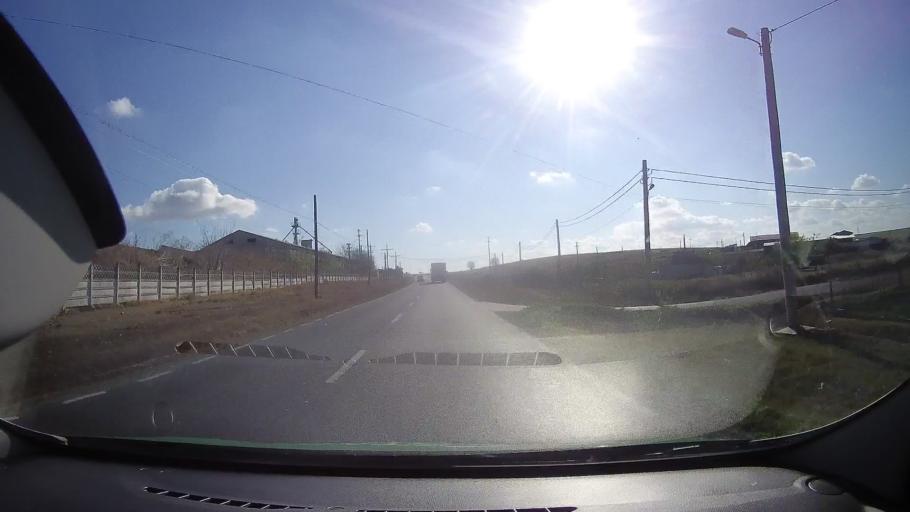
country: RO
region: Tulcea
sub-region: Comuna Baia
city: Baia
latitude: 44.7183
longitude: 28.6805
